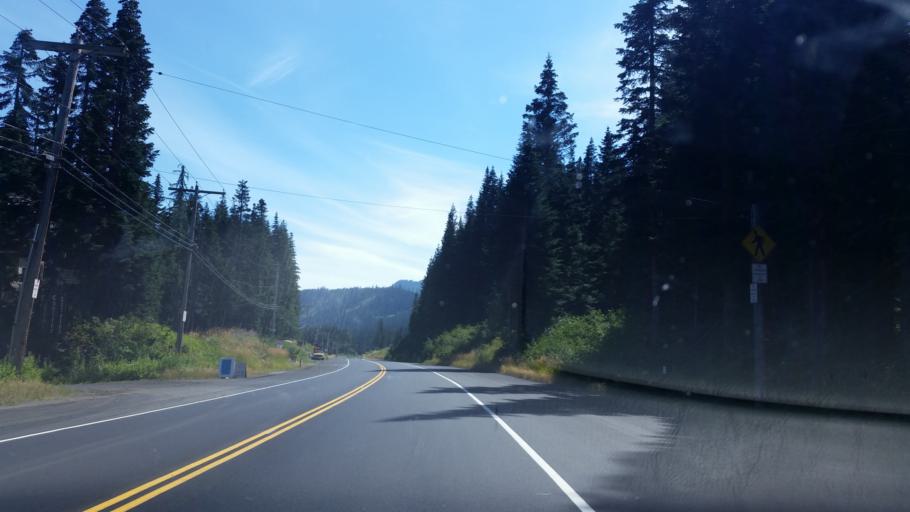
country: US
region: Washington
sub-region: King County
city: Tanner
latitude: 47.4140
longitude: -121.4135
